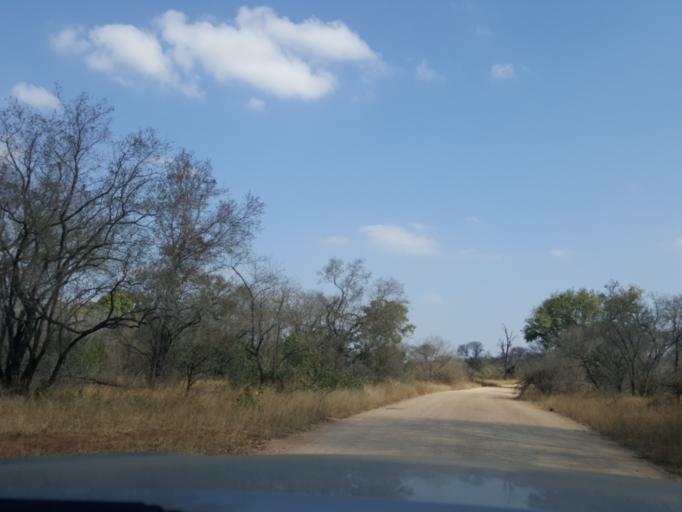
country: ZA
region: Mpumalanga
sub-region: Ehlanzeni District
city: Komatipoort
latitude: -25.2816
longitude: 31.7736
